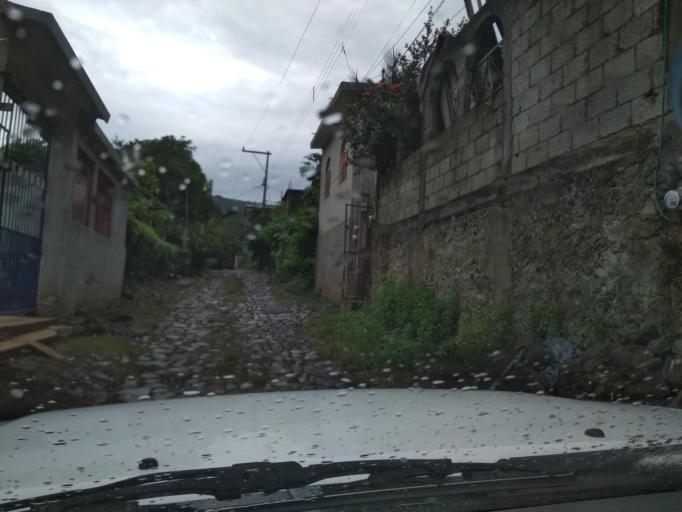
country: MX
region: Veracruz
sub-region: San Andres Tuxtla
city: San Isidro Xoteapan (San Isidro Texcaltitan)
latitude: 18.4612
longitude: -95.2349
